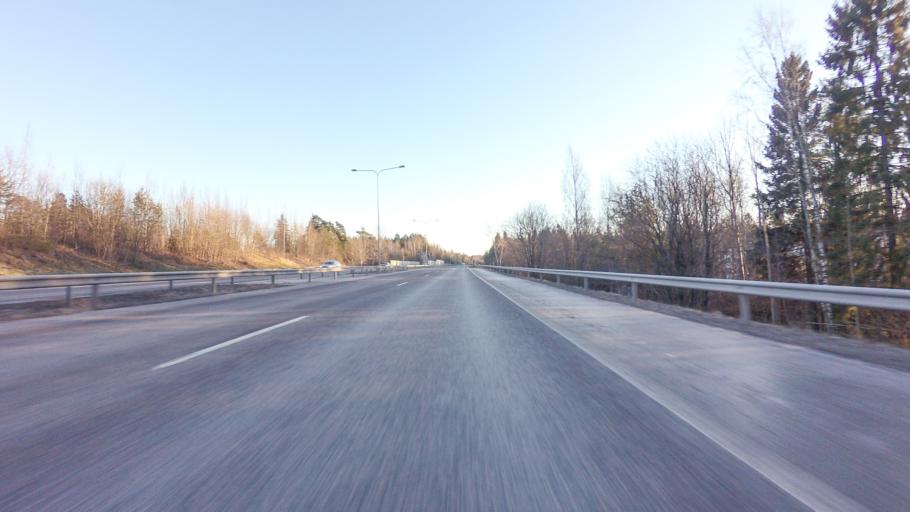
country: FI
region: Uusimaa
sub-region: Helsinki
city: Kauniainen
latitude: 60.2075
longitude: 24.6905
